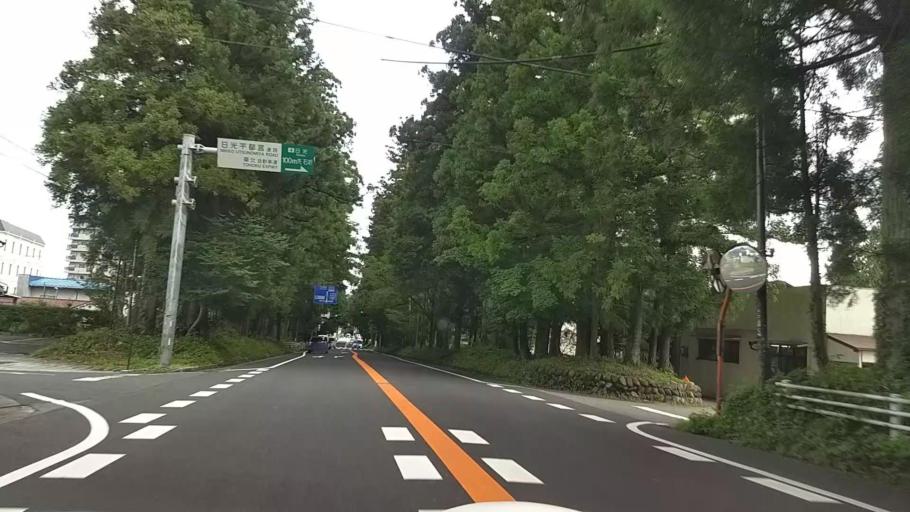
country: JP
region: Tochigi
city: Nikko
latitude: 36.7468
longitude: 139.6202
